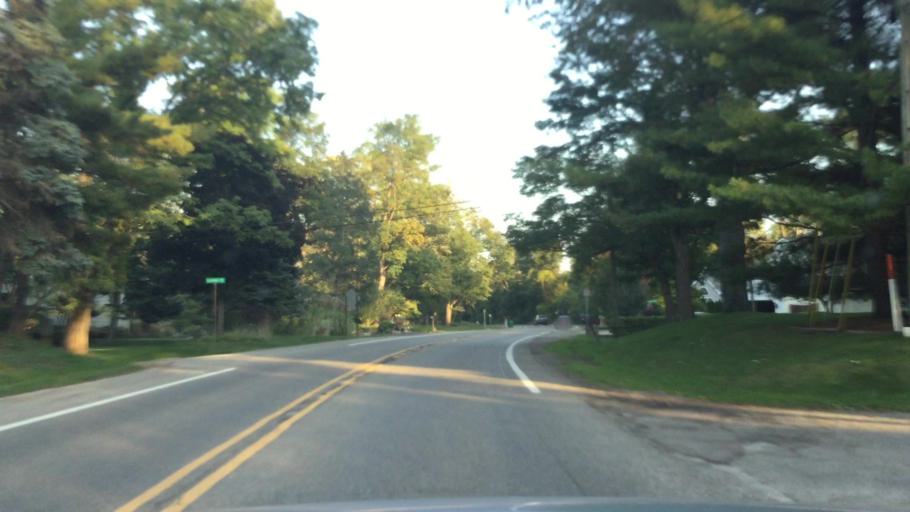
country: US
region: Michigan
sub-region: Oakland County
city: Keego Harbor
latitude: 42.6238
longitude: -83.3755
